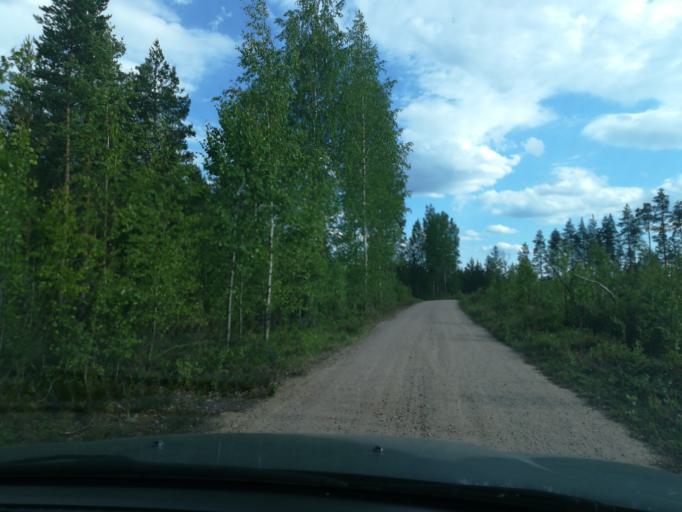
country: FI
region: Southern Savonia
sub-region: Savonlinna
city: Savonlinna
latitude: 61.6435
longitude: 28.7170
